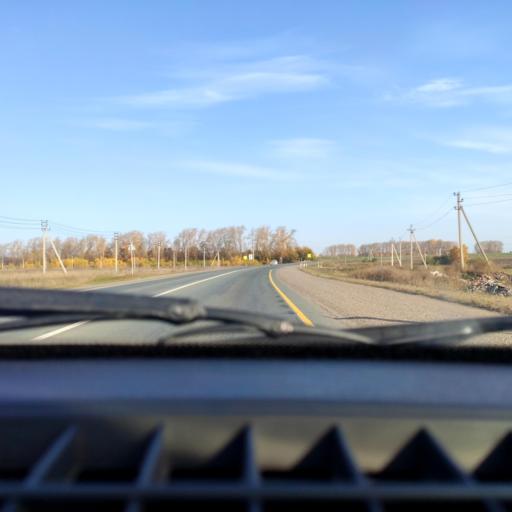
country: RU
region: Bashkortostan
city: Avdon
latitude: 54.6750
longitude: 55.7301
